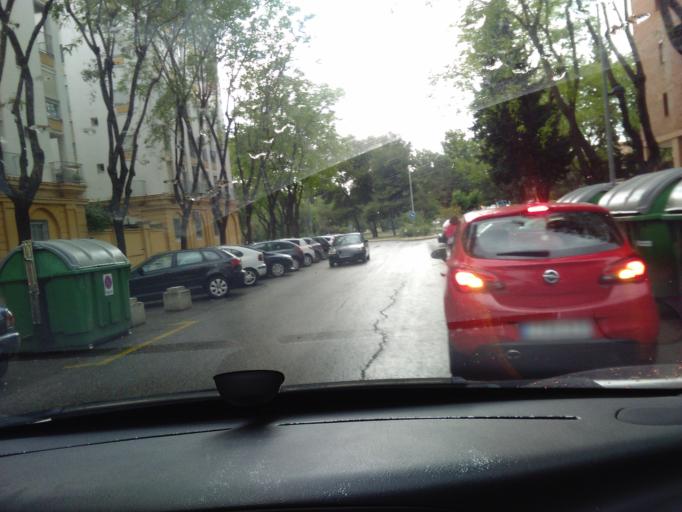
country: ES
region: Andalusia
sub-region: Provincia de Sevilla
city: Sevilla
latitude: 37.4020
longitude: -5.9399
